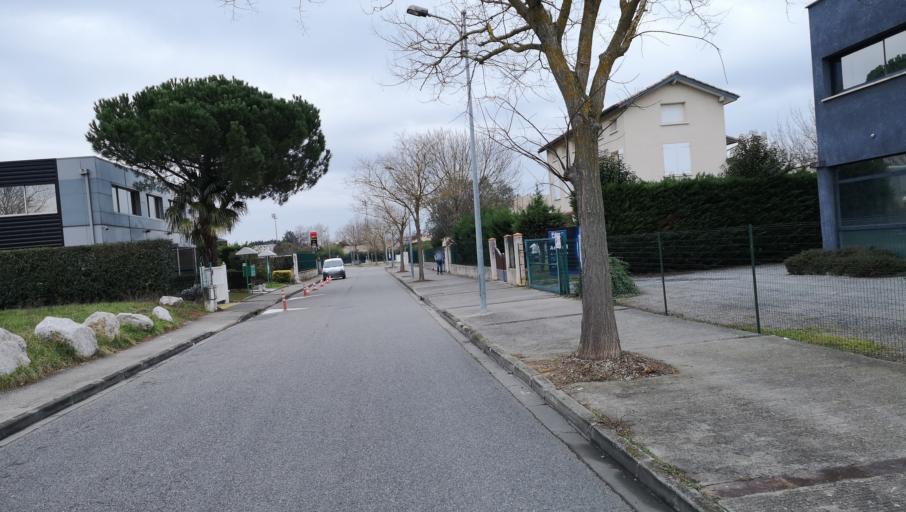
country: FR
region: Midi-Pyrenees
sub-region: Departement de la Haute-Garonne
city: Blagnac
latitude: 43.6463
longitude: 1.3820
